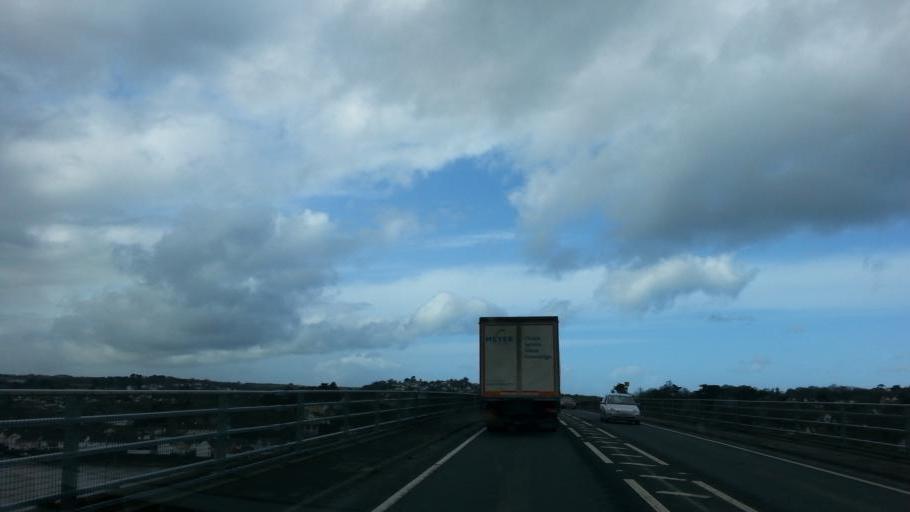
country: GB
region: England
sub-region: Devon
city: Bideford
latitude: 51.0298
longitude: -4.1980
